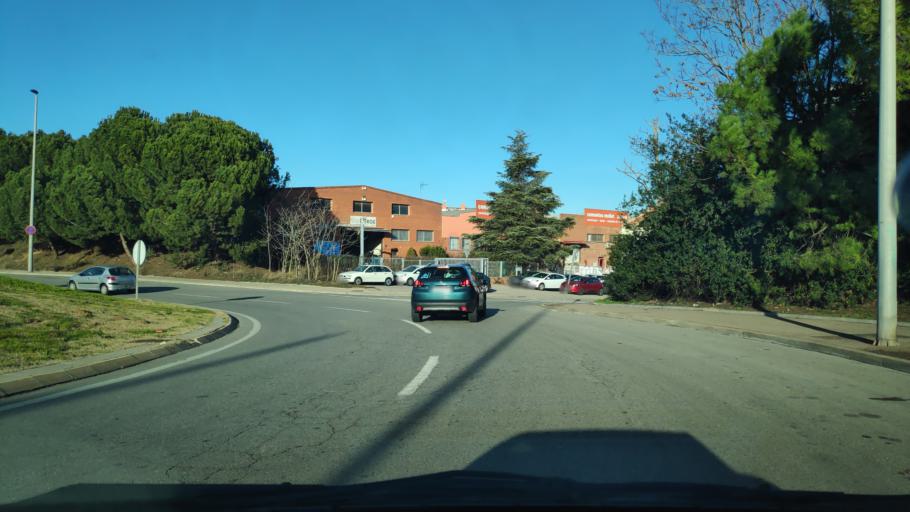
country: ES
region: Catalonia
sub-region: Provincia de Barcelona
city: Mollet del Valles
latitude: 41.5372
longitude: 2.2024
